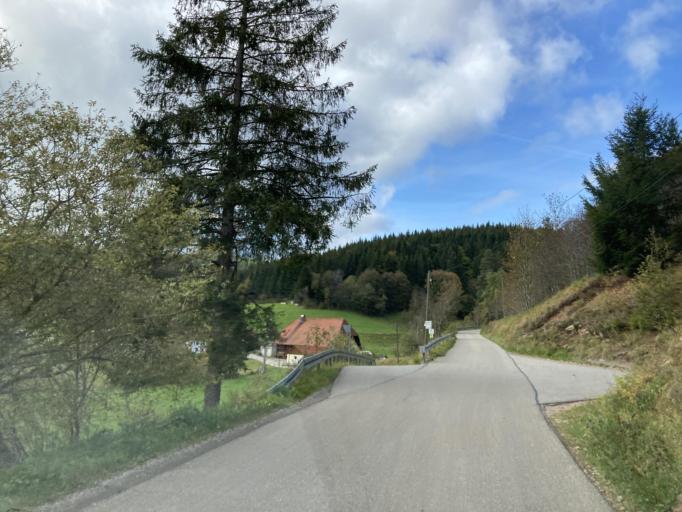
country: DE
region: Baden-Wuerttemberg
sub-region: Freiburg Region
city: Vohrenbach
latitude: 48.0583
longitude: 8.2872
